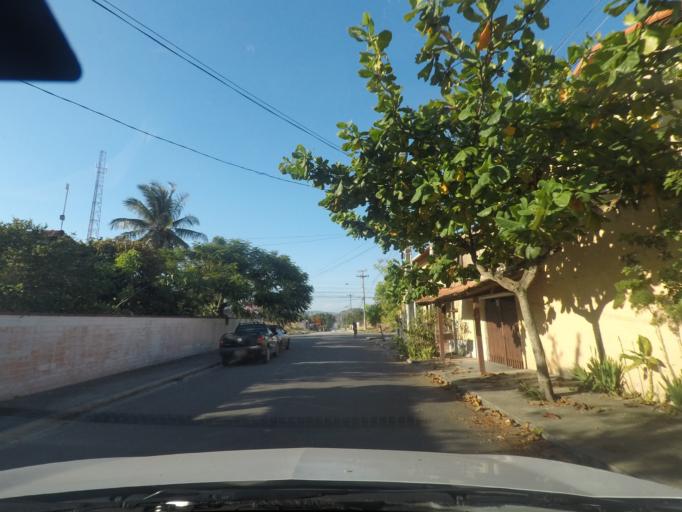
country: BR
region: Rio de Janeiro
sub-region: Marica
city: Marica
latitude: -22.9674
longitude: -42.9370
